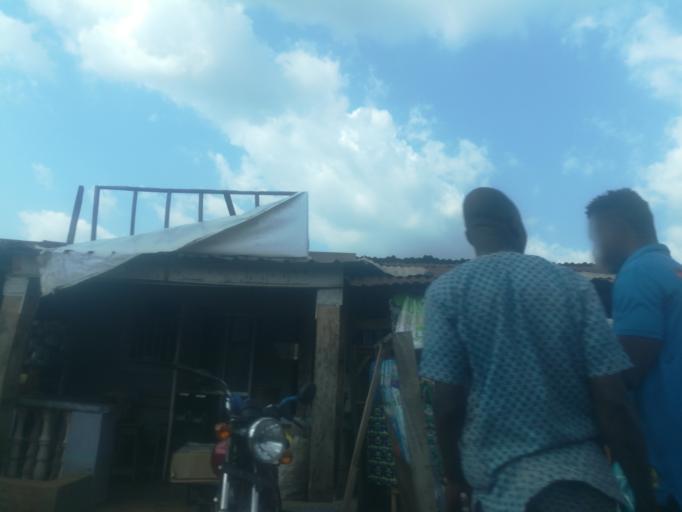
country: NG
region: Oyo
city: Moniya
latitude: 7.5130
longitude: 3.9123
